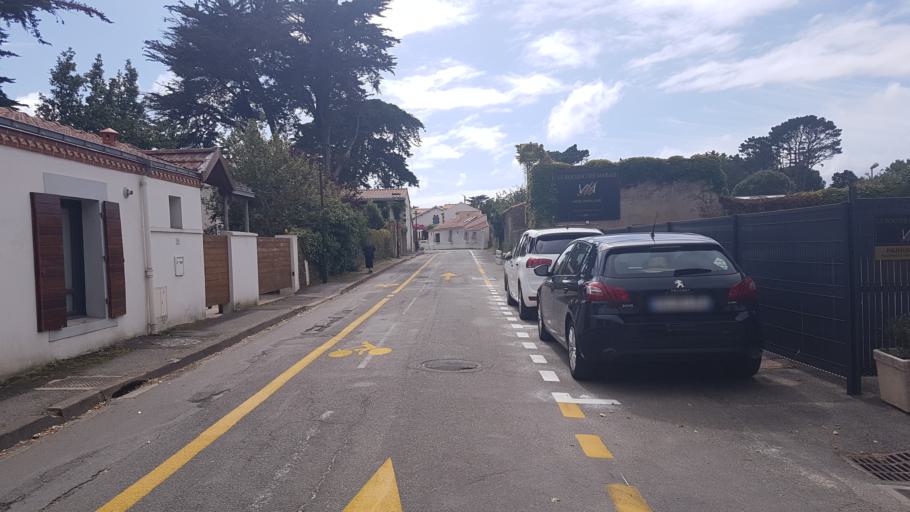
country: FR
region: Pays de la Loire
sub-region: Departement de la Loire-Atlantique
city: Pornic
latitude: 47.1124
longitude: -2.1345
